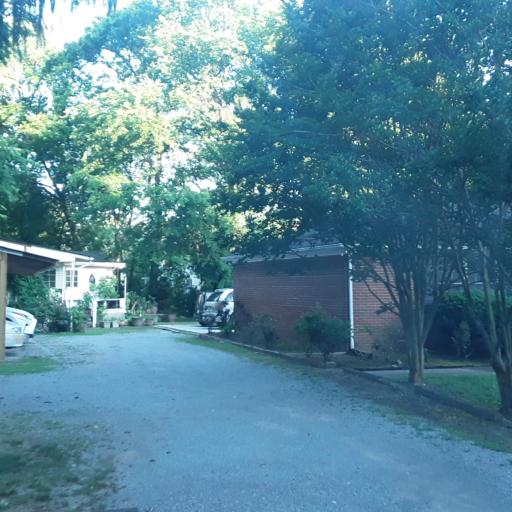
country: US
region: Tennessee
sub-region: Davidson County
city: Oak Hill
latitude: 36.1028
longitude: -86.7321
